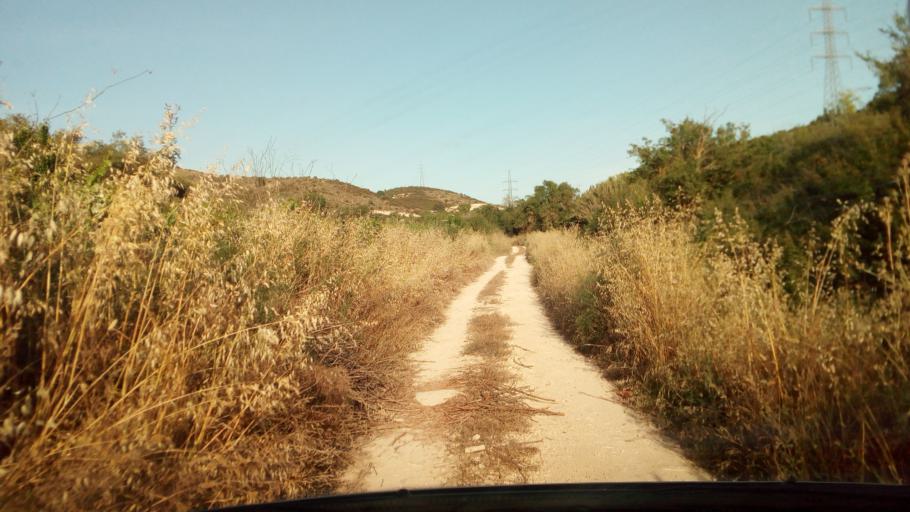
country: CY
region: Pafos
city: Tala
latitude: 34.8719
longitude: 32.4742
